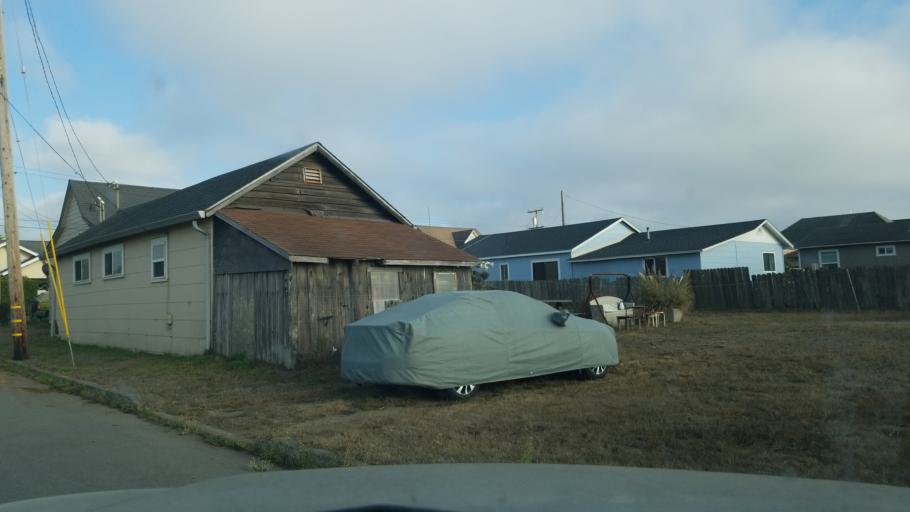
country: US
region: California
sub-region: Mendocino County
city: Fort Bragg
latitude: 39.4493
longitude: -123.8092
